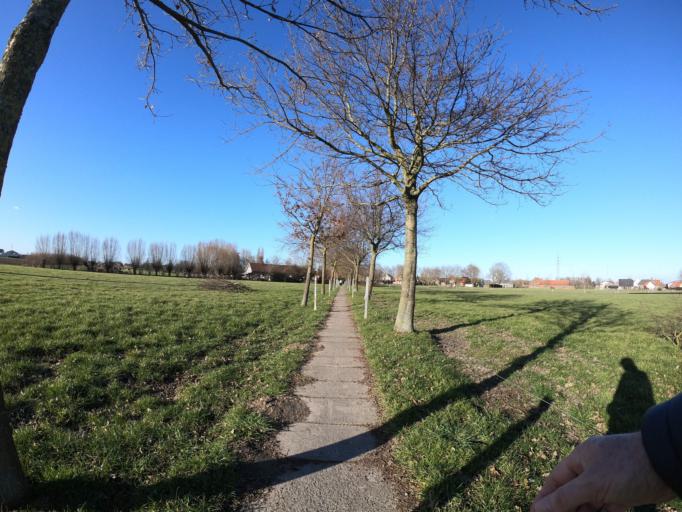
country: BE
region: Flanders
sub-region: Provincie West-Vlaanderen
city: Avelgem
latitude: 50.7827
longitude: 3.4430
